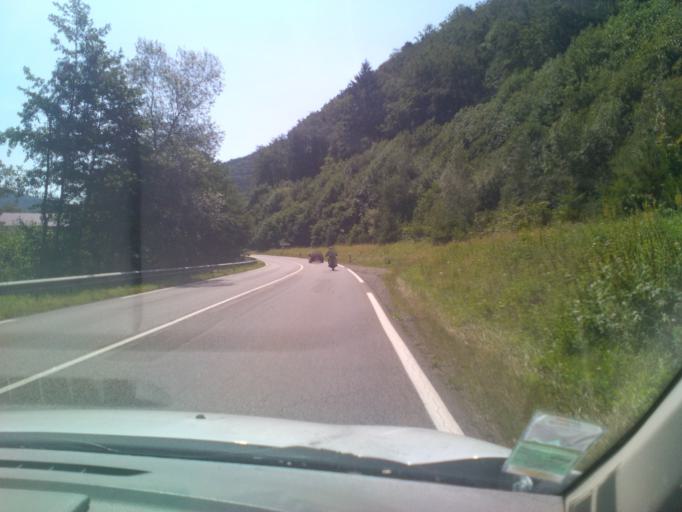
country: FR
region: Alsace
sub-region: Departement du Haut-Rhin
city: Freland
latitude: 48.1558
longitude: 7.2278
